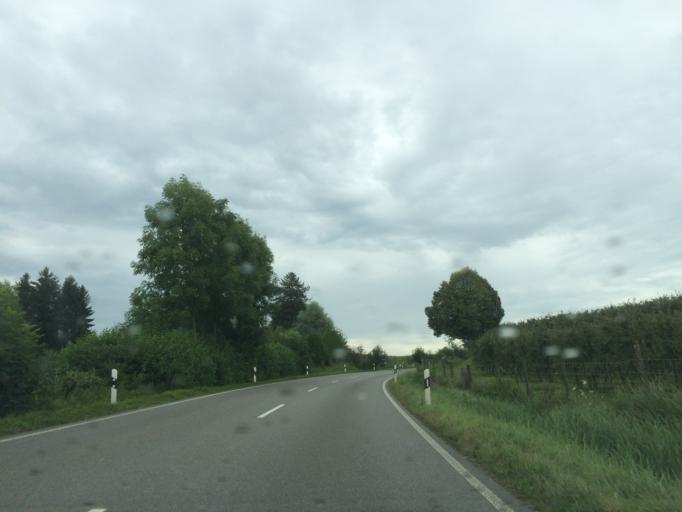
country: DE
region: Baden-Wuerttemberg
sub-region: Tuebingen Region
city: Oberteuringen
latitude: 47.7455
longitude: 9.4887
